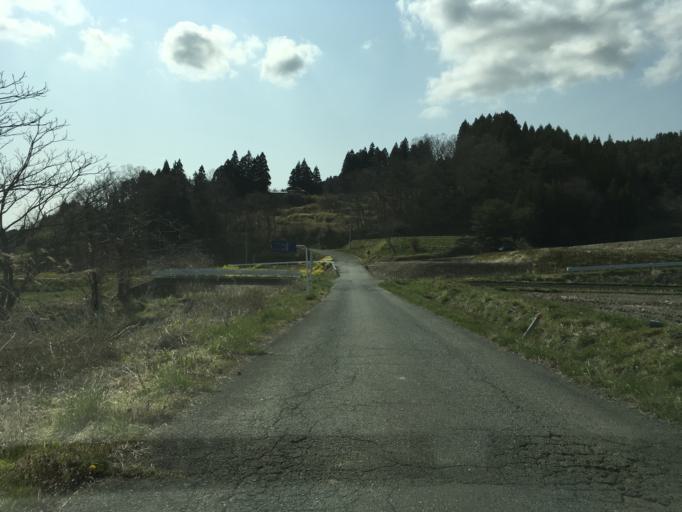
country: JP
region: Iwate
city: Ichinoseki
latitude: 38.8480
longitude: 141.3614
